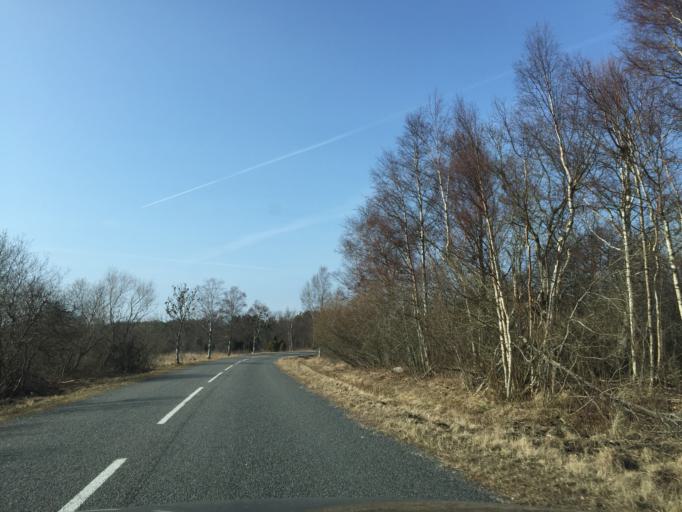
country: LV
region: Dundaga
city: Dundaga
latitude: 57.9193
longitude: 22.0544
